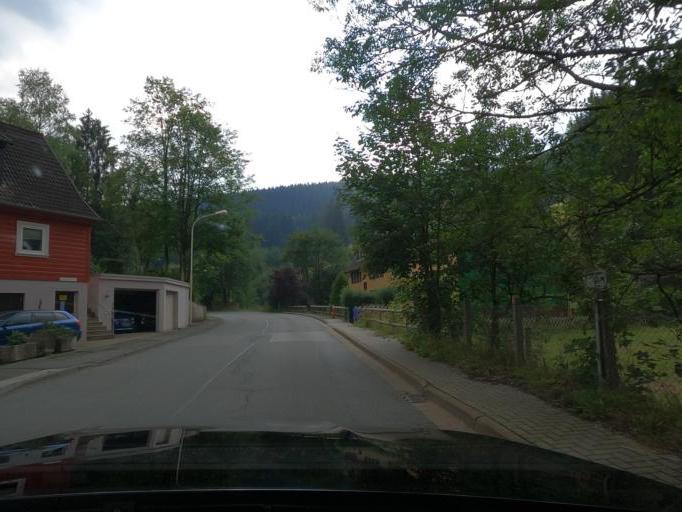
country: DE
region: Lower Saxony
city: Wildemann
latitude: 51.8218
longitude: 10.2717
